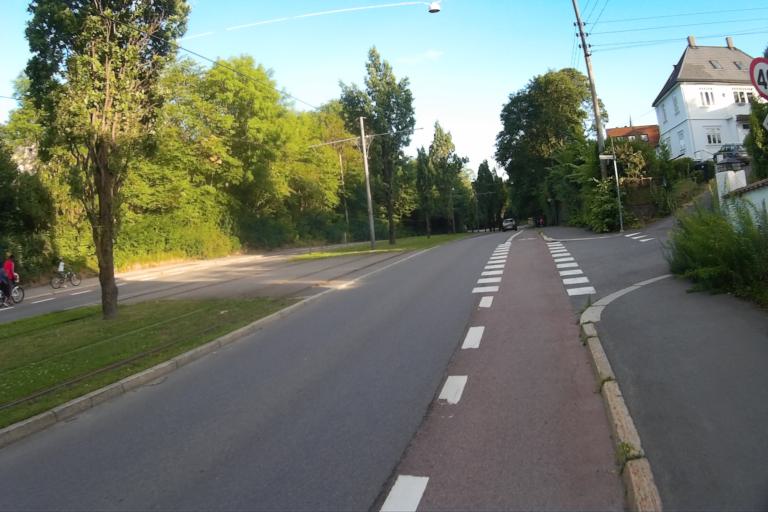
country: NO
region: Oslo
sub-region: Oslo
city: Oslo
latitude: 59.9395
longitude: 10.7297
